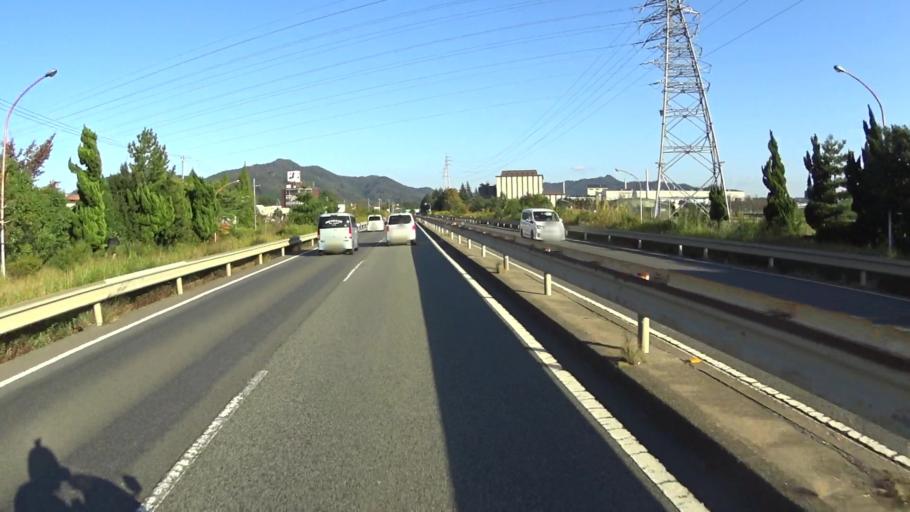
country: JP
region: Kyoto
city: Fukuchiyama
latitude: 35.2885
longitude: 135.1710
